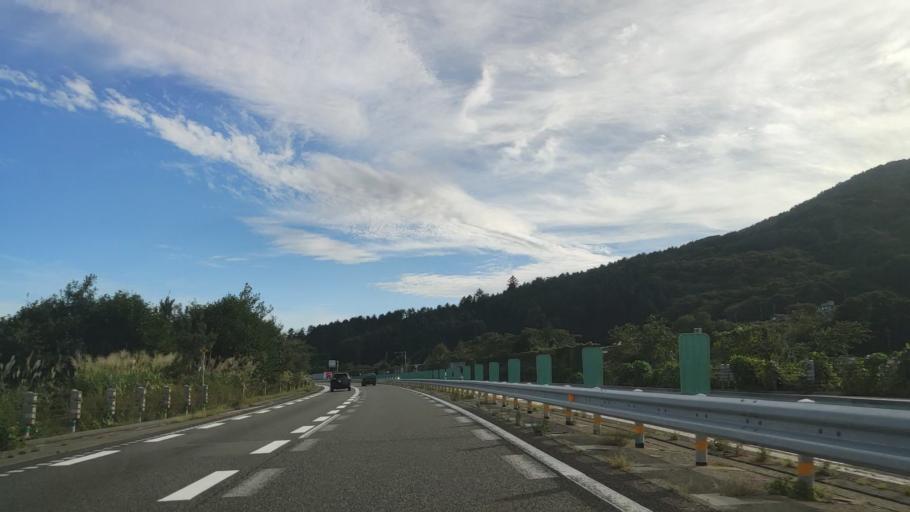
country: JP
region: Nagano
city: Ina
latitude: 35.8342
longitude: 137.9282
